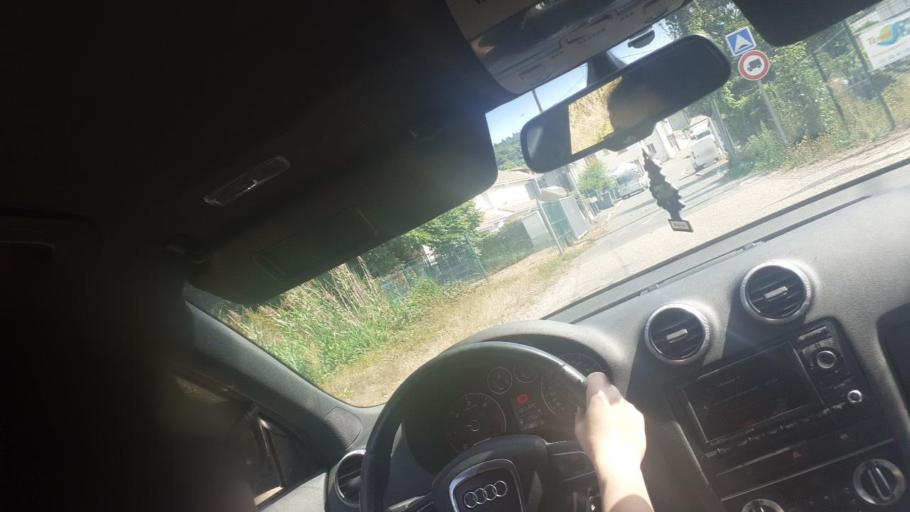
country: FR
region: Haute-Normandie
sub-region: Departement de la Seine-Maritime
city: Grand-Couronne
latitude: 49.3631
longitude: 1.0075
